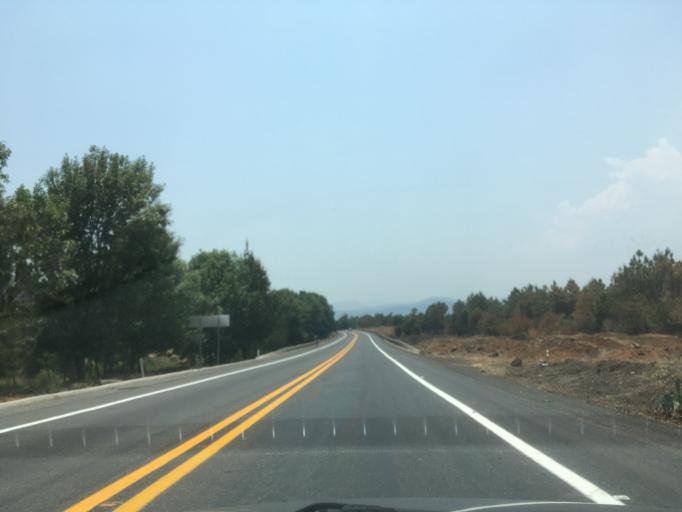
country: MX
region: Michoacan
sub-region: Patzcuaro
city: Santa Ana Chapitiro
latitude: 19.5067
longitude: -101.6647
